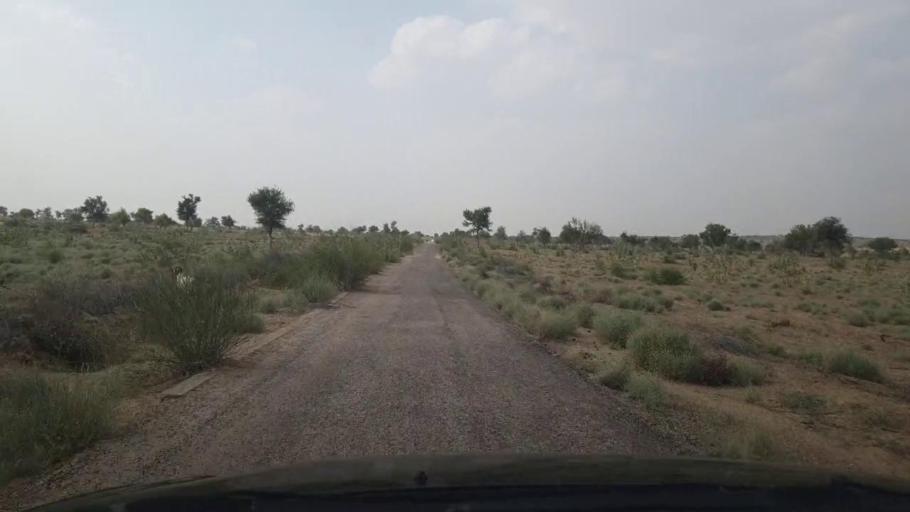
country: PK
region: Sindh
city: Islamkot
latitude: 24.9734
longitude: 70.5876
